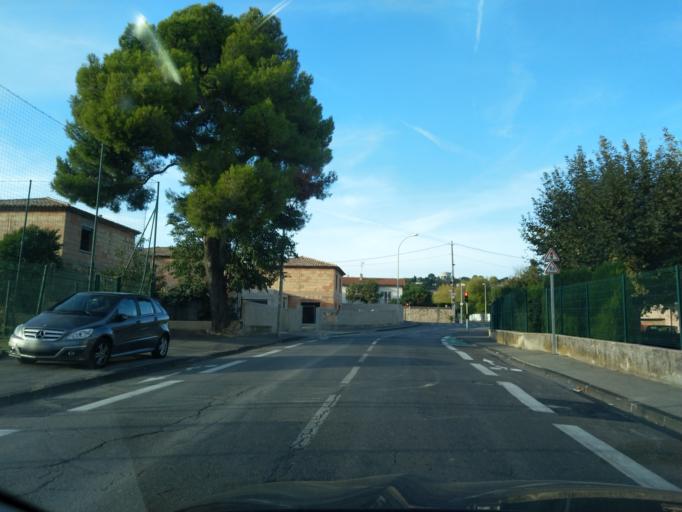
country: FR
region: Provence-Alpes-Cote d'Azur
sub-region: Departement des Bouches-du-Rhone
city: Marseille 12
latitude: 43.3024
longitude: 5.4497
